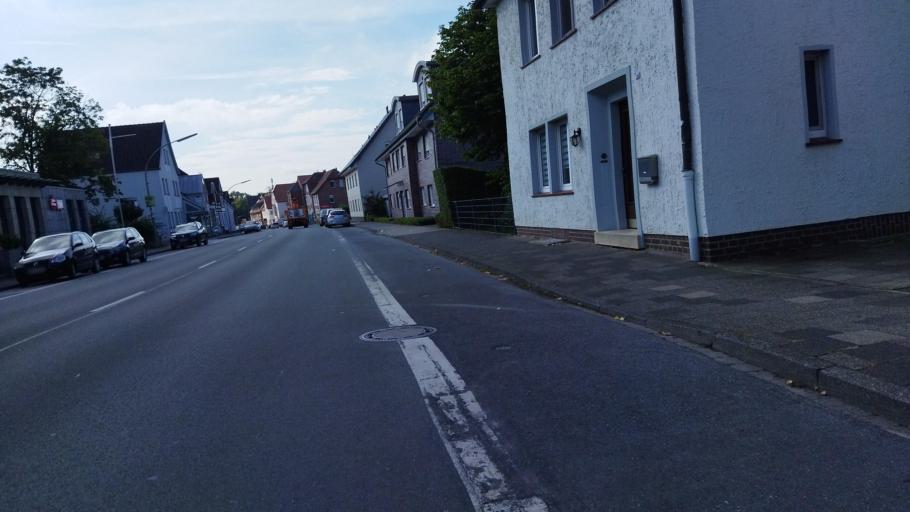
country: DE
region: North Rhine-Westphalia
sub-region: Regierungsbezirk Munster
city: Warendorf
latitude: 51.9582
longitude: 7.9929
